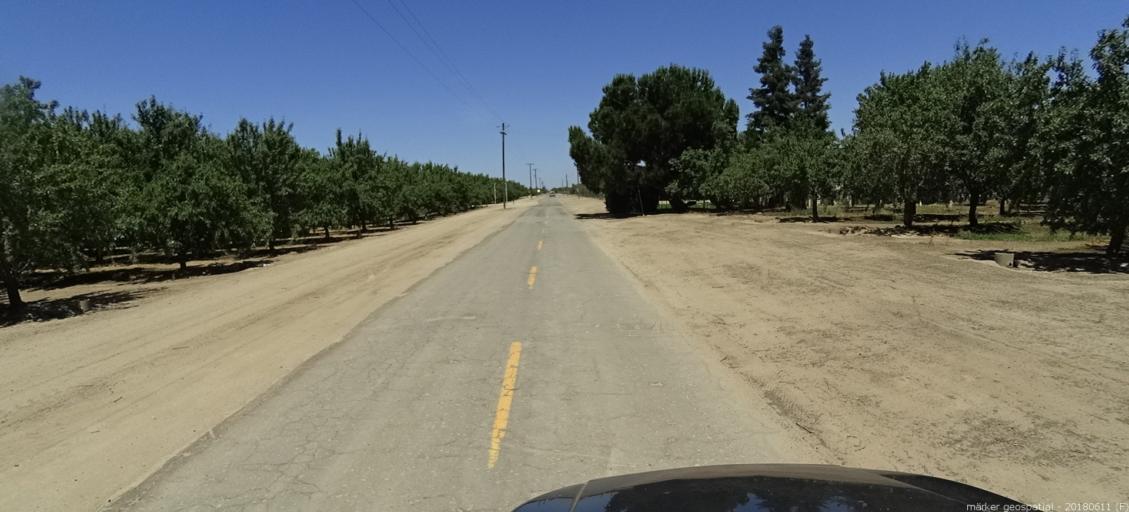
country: US
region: California
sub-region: Madera County
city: Fairmead
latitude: 37.0234
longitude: -120.1932
